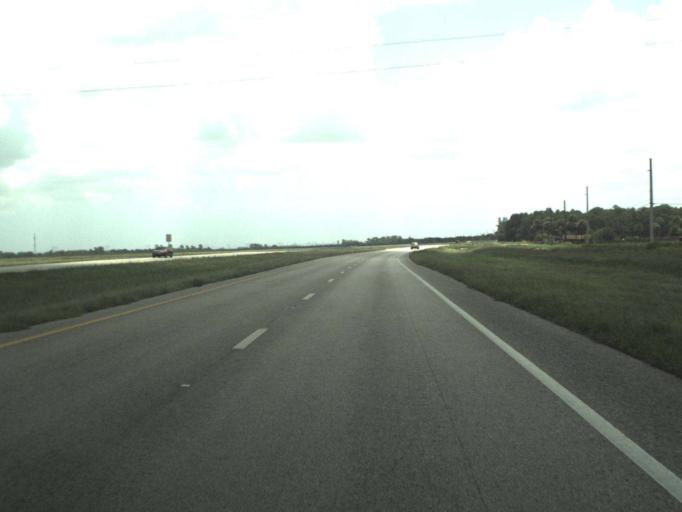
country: US
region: Florida
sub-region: Saint Lucie County
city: Fort Pierce South
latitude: 27.3670
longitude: -80.5264
